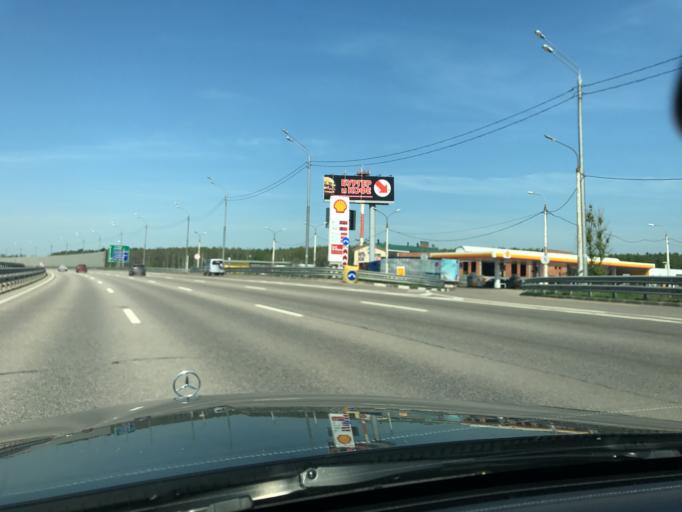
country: RU
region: Moskovskaya
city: Rozhdestveno
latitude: 55.8171
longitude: 37.0197
